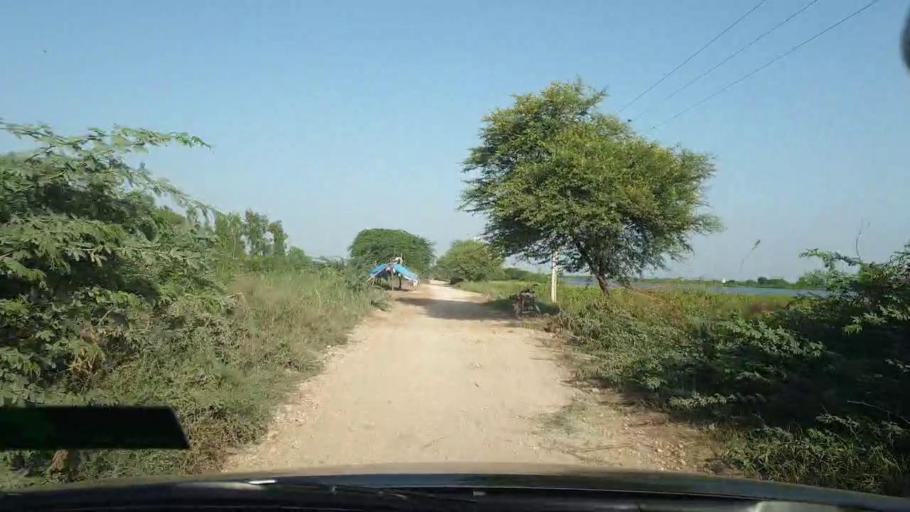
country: PK
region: Sindh
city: Naukot
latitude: 24.7407
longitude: 69.2325
